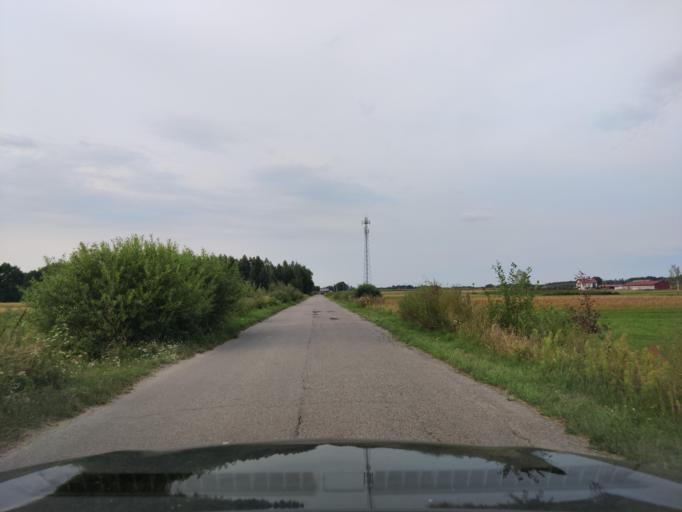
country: PL
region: Masovian Voivodeship
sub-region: Powiat pultuski
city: Obryte
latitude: 52.7321
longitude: 21.2469
